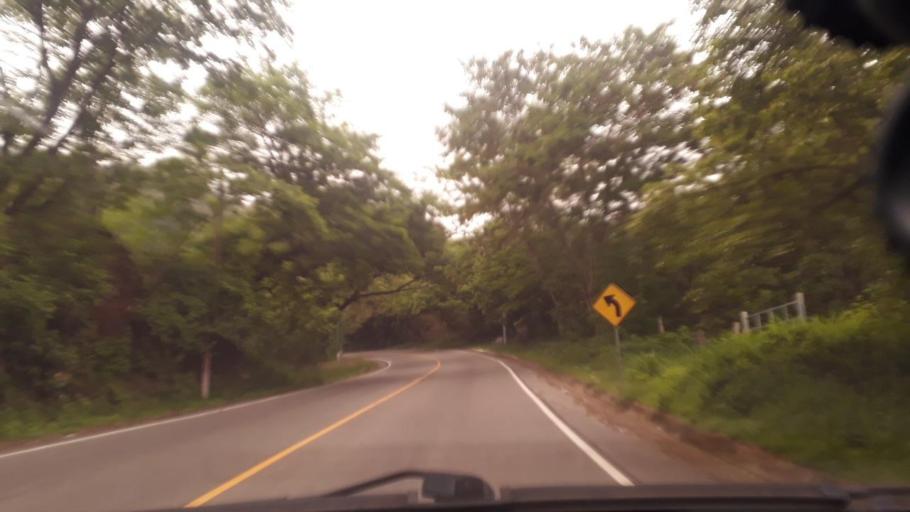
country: GT
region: Chiquimula
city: San Jacinto
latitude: 14.6474
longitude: -89.4833
